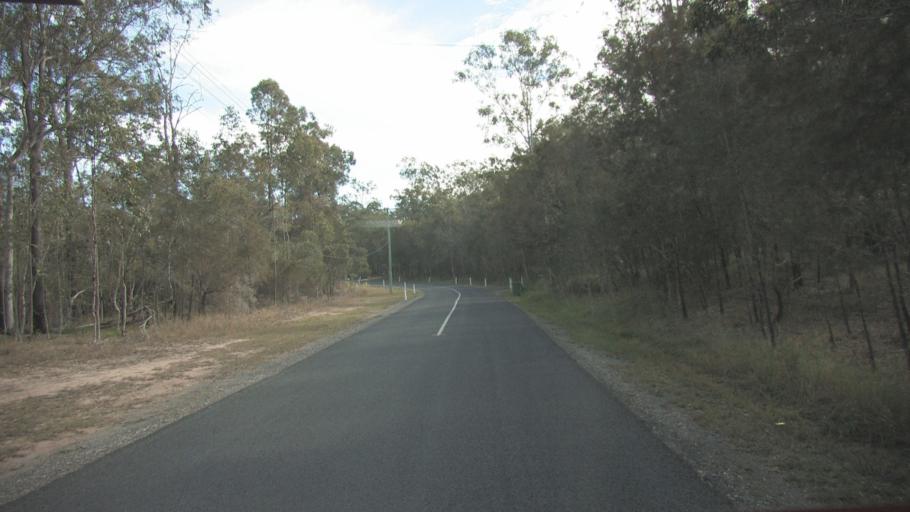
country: AU
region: Queensland
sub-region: Logan
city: North Maclean
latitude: -27.7766
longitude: 152.9679
